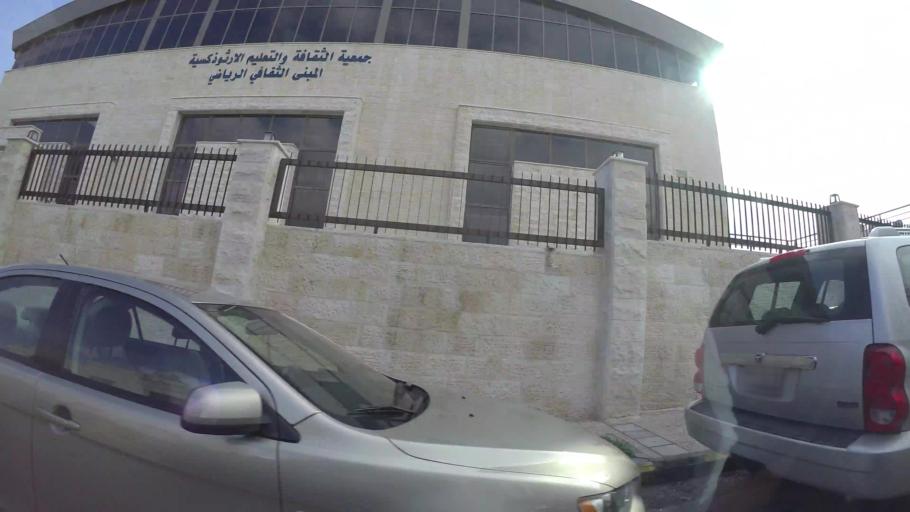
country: JO
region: Amman
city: Amman
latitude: 31.9642
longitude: 35.8938
